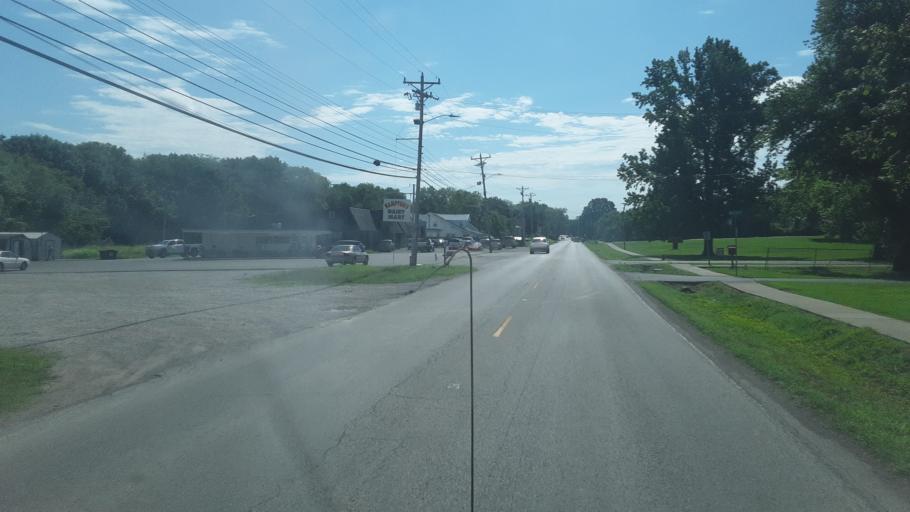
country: US
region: Kentucky
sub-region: Todd County
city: Elkton
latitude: 36.8116
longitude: -87.1634
